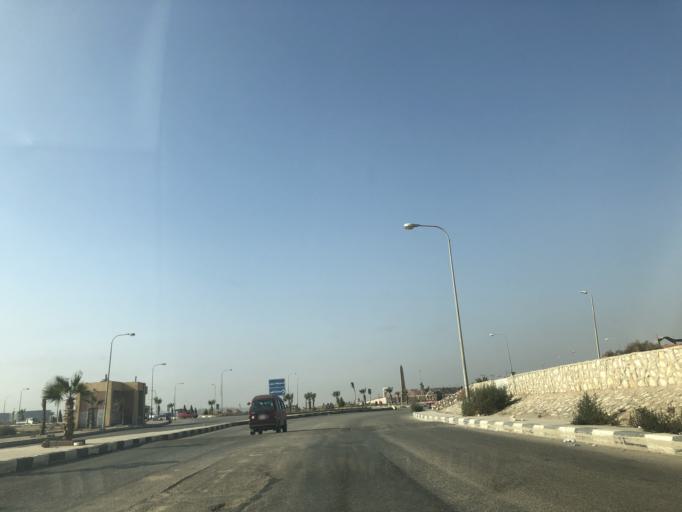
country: EG
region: Al Jizah
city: Madinat Sittah Uktubar
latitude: 29.9322
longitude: 31.0450
